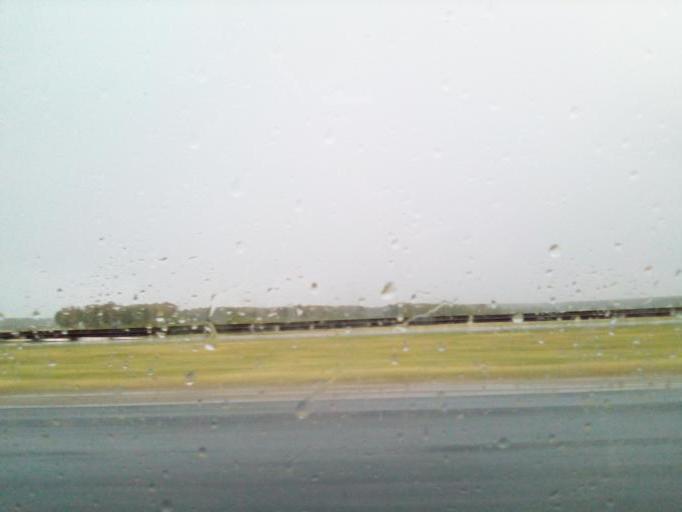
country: RU
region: Chelyabinsk
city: Poletayevo
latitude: 54.9769
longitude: 60.9916
